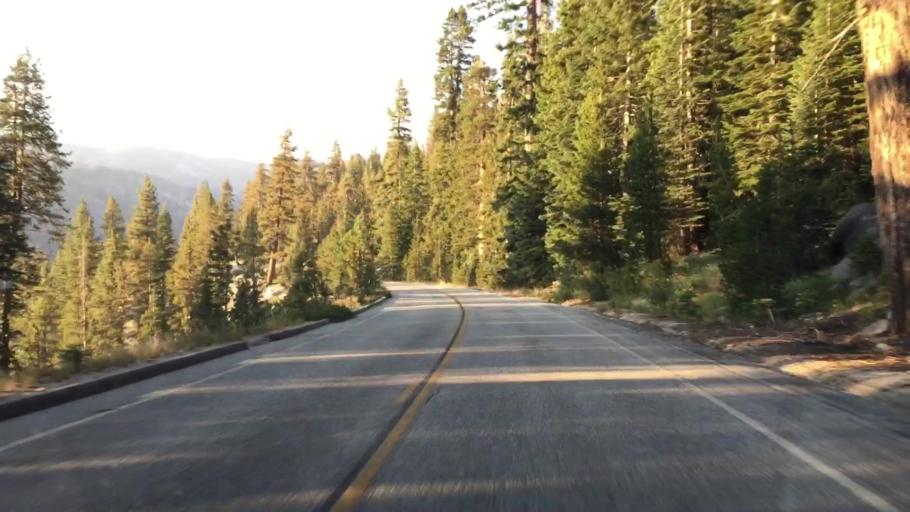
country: US
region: California
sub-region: Mariposa County
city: Yosemite Valley
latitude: 37.8323
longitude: -119.5784
